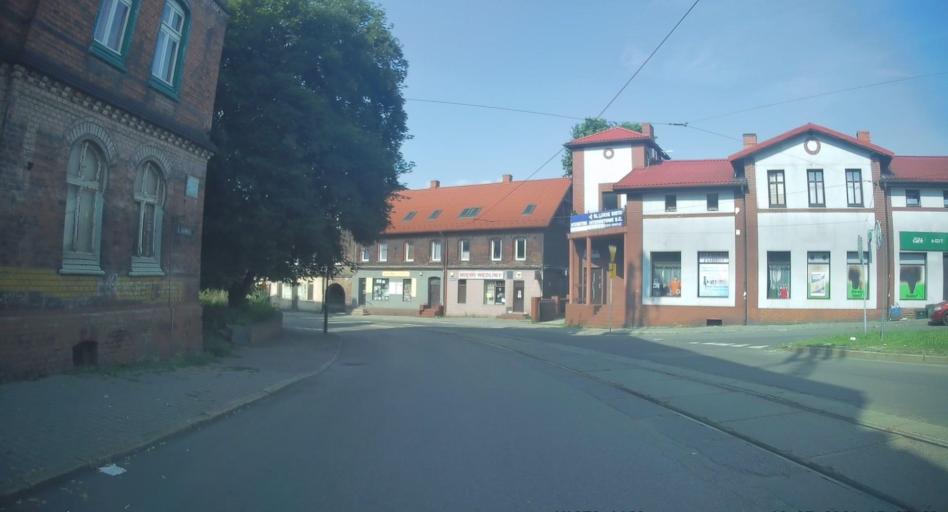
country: PL
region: Silesian Voivodeship
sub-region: Swietochlowice
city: Swietochlowice
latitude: 50.3118
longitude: 18.9143
